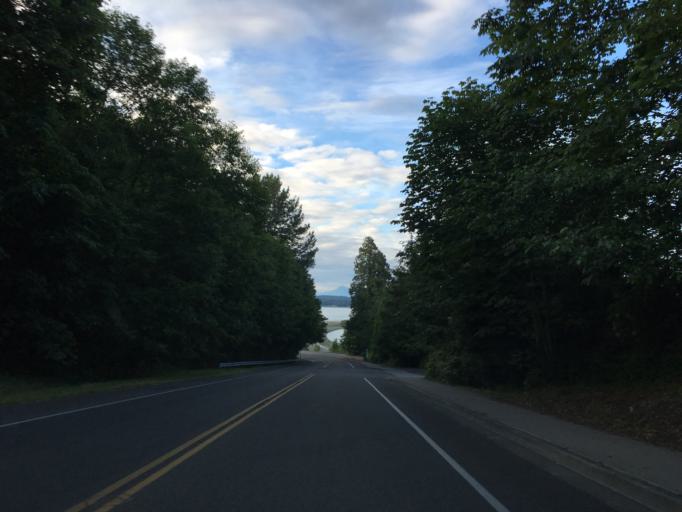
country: CA
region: British Columbia
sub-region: Greater Vancouver Regional District
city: White Rock
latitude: 48.9753
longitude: -122.7921
